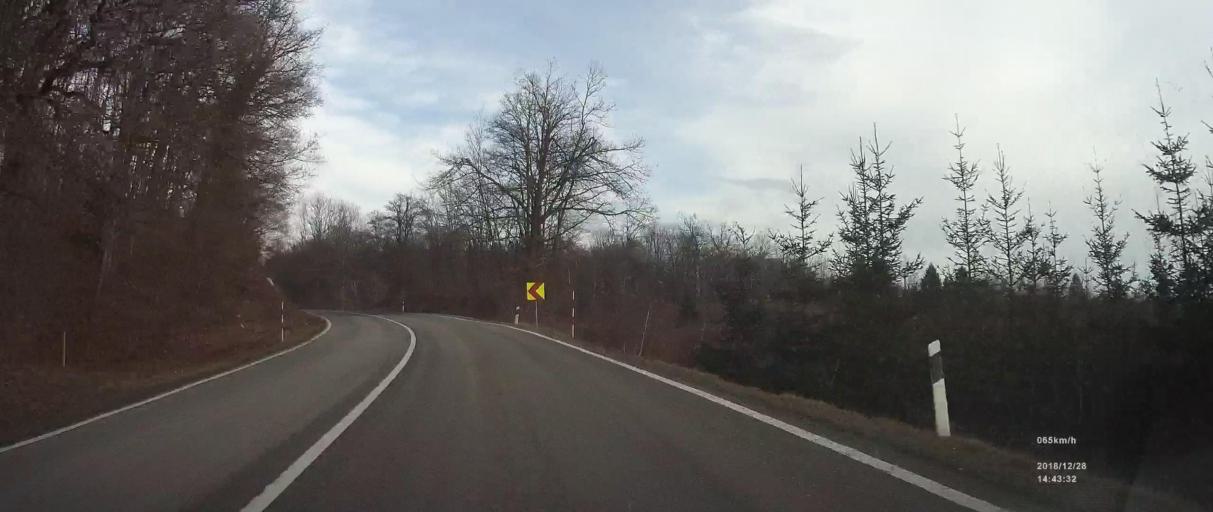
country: SI
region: Crnomelj
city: Crnomelj
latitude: 45.4465
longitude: 15.2802
